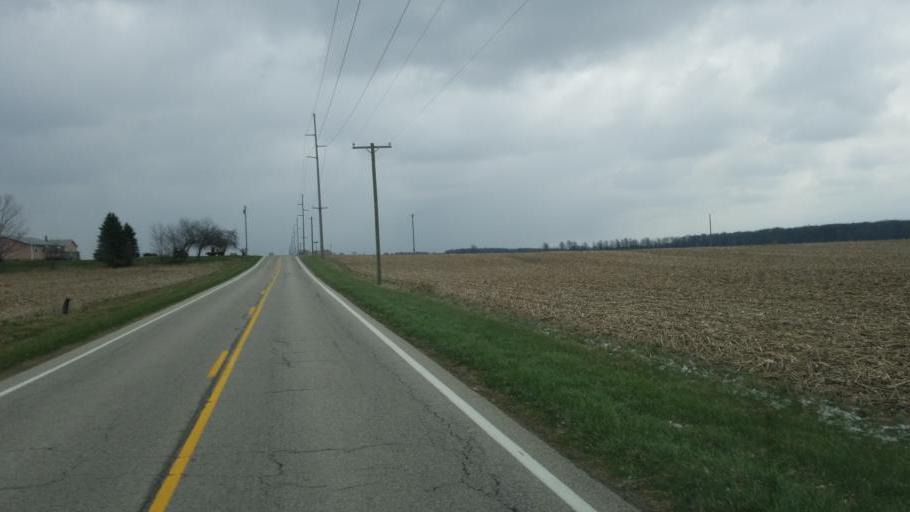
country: US
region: Ohio
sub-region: Union County
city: Richwood
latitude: 40.4514
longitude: -83.3681
